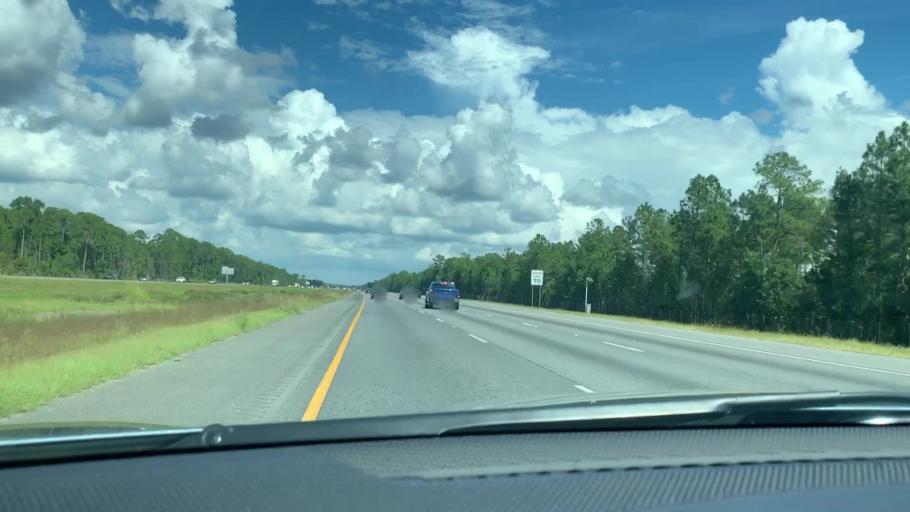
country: US
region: Georgia
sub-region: Camden County
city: Woodbine
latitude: 31.0640
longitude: -81.6314
